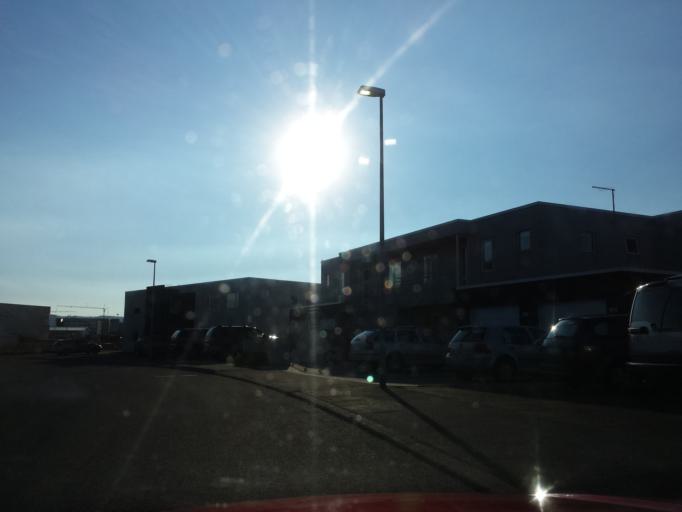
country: IS
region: Capital Region
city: Reykjavik
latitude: 64.0861
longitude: -21.8299
